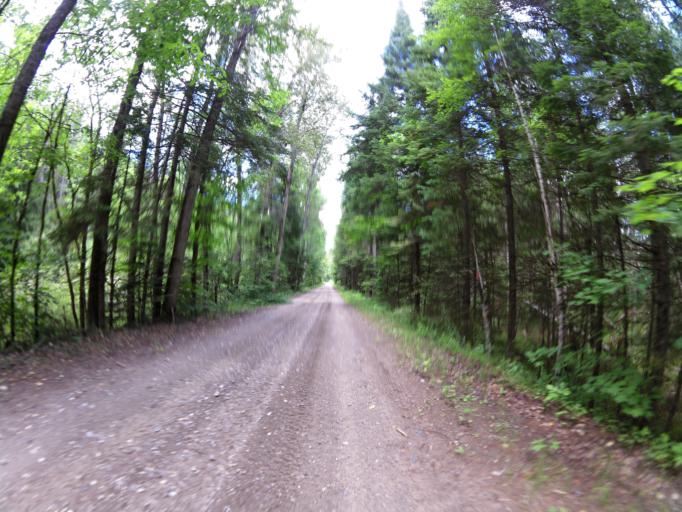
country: CA
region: Ontario
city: Renfrew
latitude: 45.1159
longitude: -76.6928
